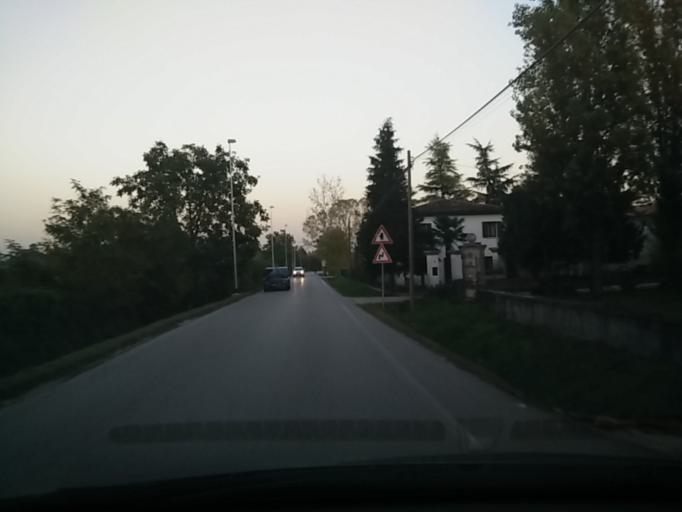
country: IT
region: Veneto
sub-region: Provincia di Treviso
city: Varago
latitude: 45.7210
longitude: 12.2949
